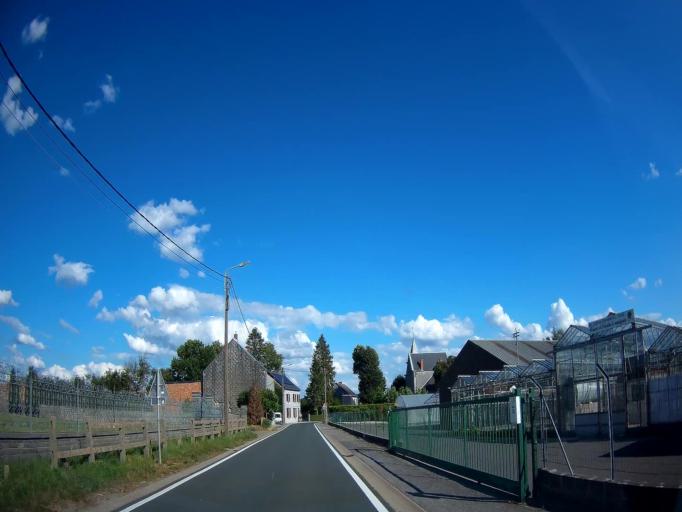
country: BE
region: Wallonia
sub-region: Province de Namur
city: Mettet
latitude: 50.3204
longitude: 4.7459
